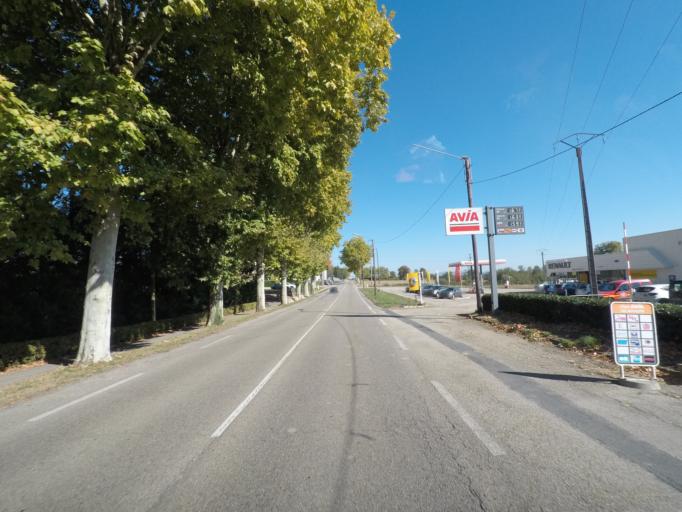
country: FR
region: Rhone-Alpes
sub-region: Departement de l'Ain
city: Servas
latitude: 46.1351
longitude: 5.1669
